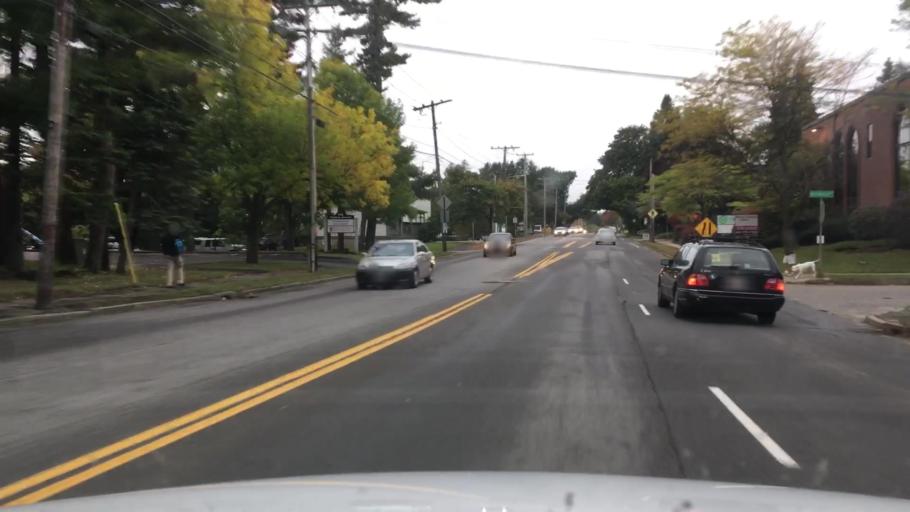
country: US
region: Maine
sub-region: Cumberland County
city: South Portland Gardens
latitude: 43.6694
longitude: -70.3033
